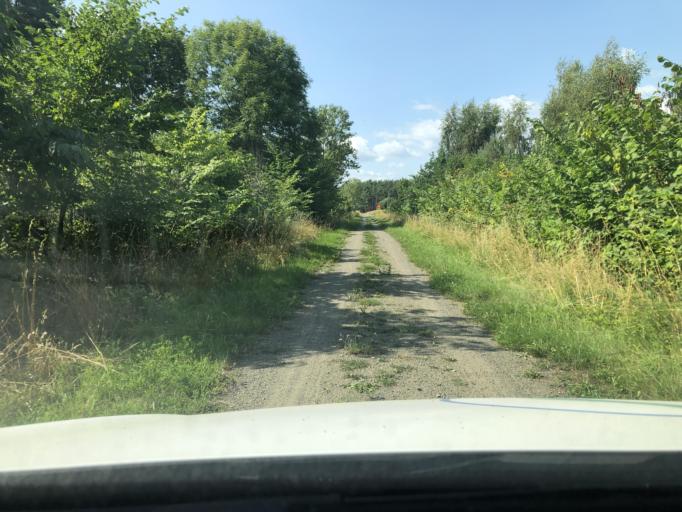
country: SE
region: Skane
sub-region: Kristianstads Kommun
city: Degeberga
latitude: 55.8116
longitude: 14.1314
